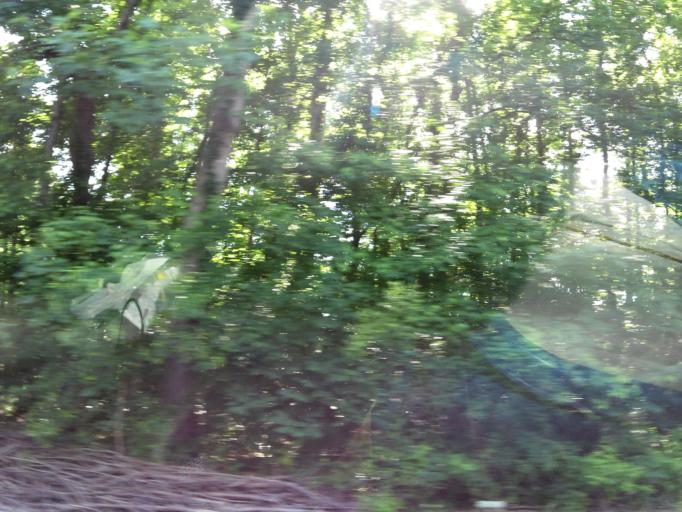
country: US
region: Tennessee
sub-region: Gibson County
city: Milan
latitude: 35.9731
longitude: -88.7160
